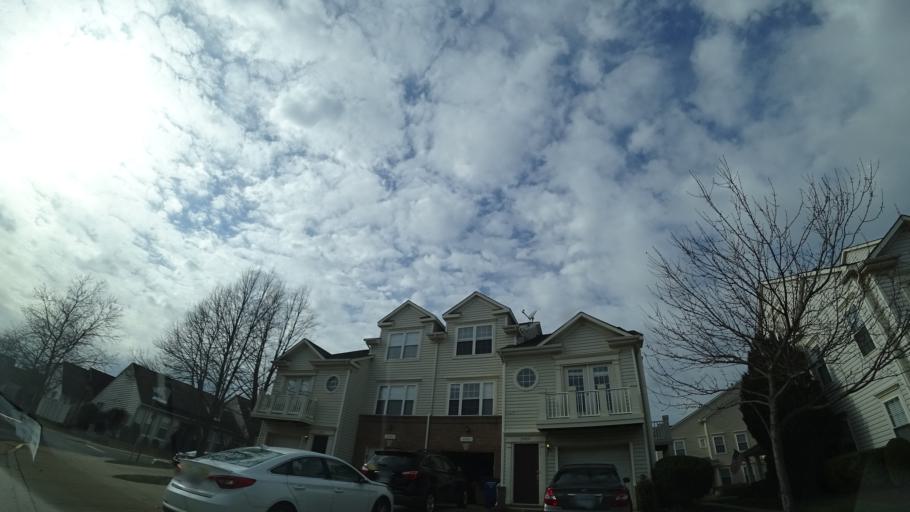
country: US
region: Virginia
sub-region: Loudoun County
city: Belmont
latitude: 39.0510
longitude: -77.5028
